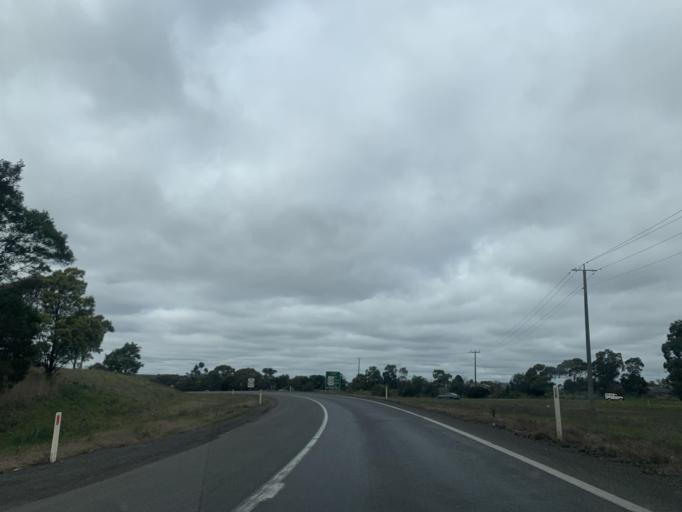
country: AU
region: Victoria
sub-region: Ballarat North
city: Lake Wendouree
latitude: -37.5165
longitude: 143.8278
